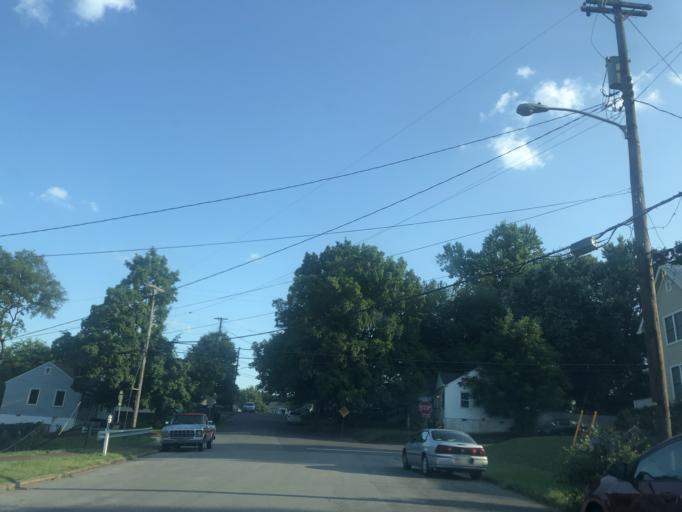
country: US
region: Tennessee
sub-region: Davidson County
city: Nashville
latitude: 36.1655
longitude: -86.7488
